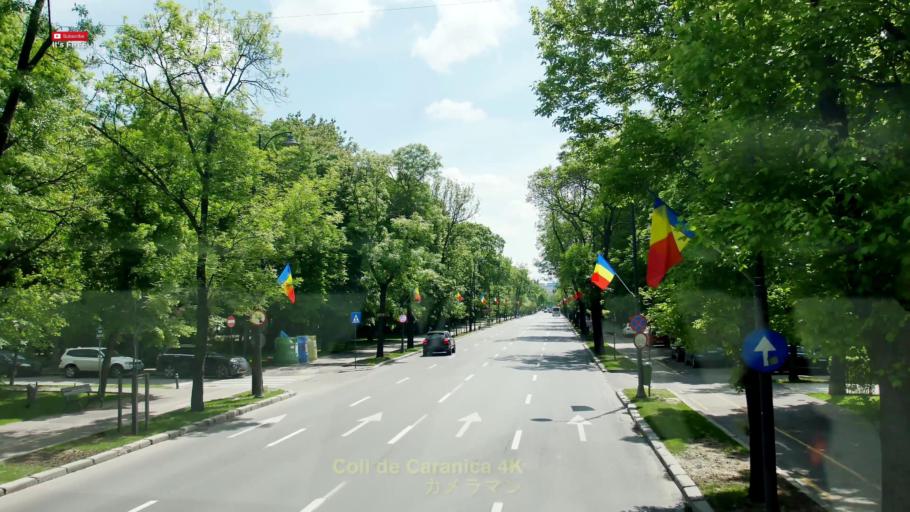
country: RO
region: Bucuresti
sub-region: Municipiul Bucuresti
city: Bucuresti
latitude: 44.4646
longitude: 26.0793
